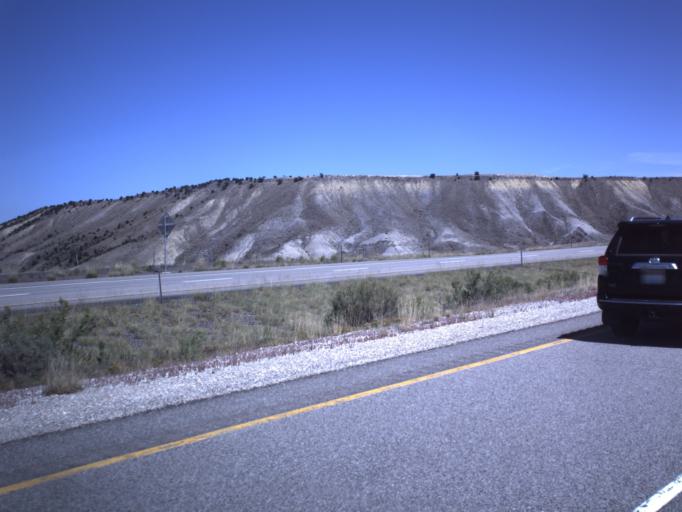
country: US
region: Utah
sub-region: Emery County
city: Ferron
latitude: 38.7655
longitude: -111.3521
